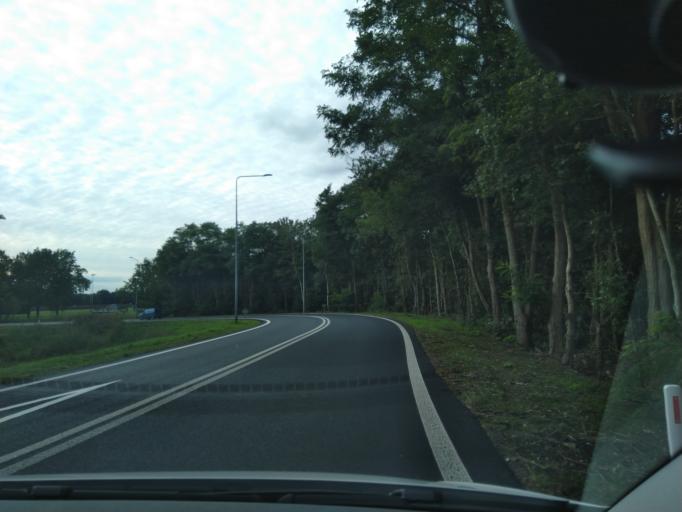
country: NL
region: Groningen
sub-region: Gemeente Veendam
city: Veendam
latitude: 53.0947
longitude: 6.9128
